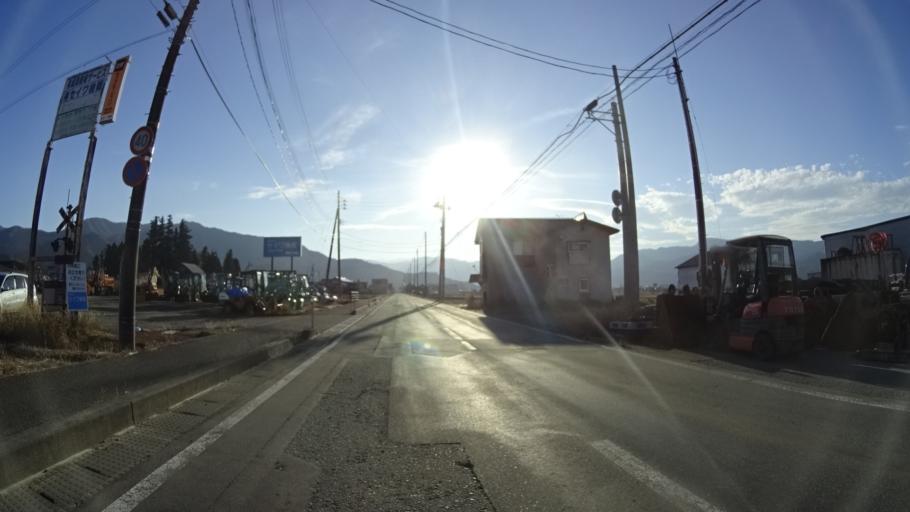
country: JP
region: Niigata
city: Shiozawa
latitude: 37.0204
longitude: 138.8623
